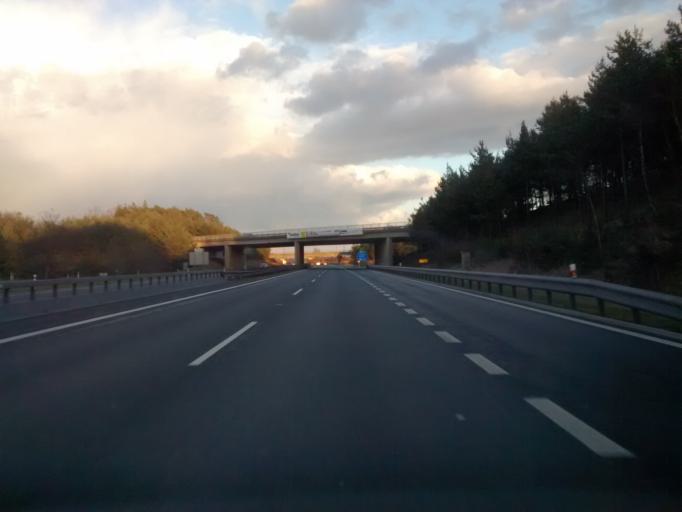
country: CZ
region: Central Bohemia
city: Poricany
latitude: 50.1195
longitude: 14.9405
